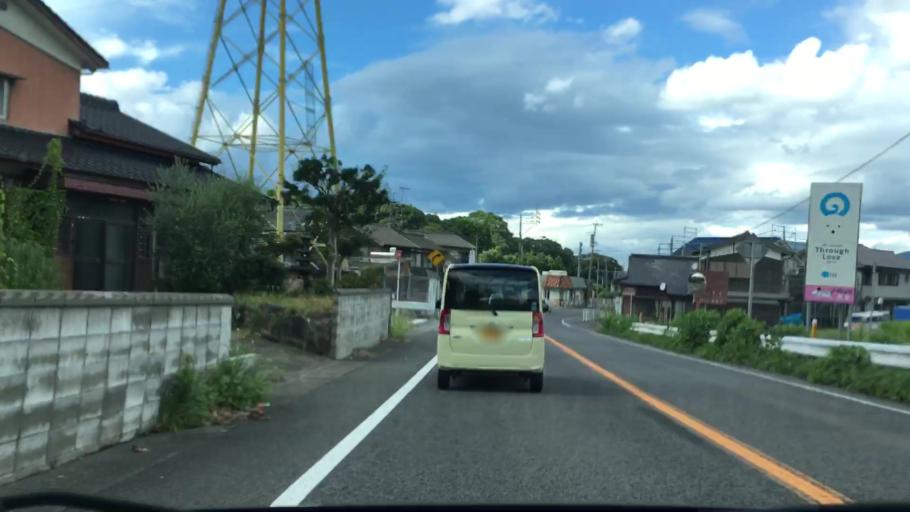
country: JP
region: Saga Prefecture
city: Imaricho-ko
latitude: 33.1780
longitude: 129.8520
